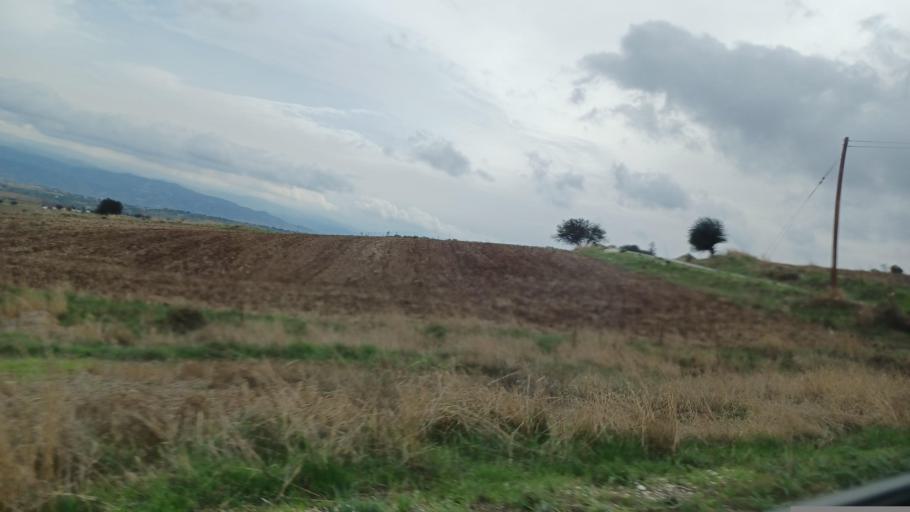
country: CY
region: Pafos
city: Polis
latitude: 34.9878
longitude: 32.3792
